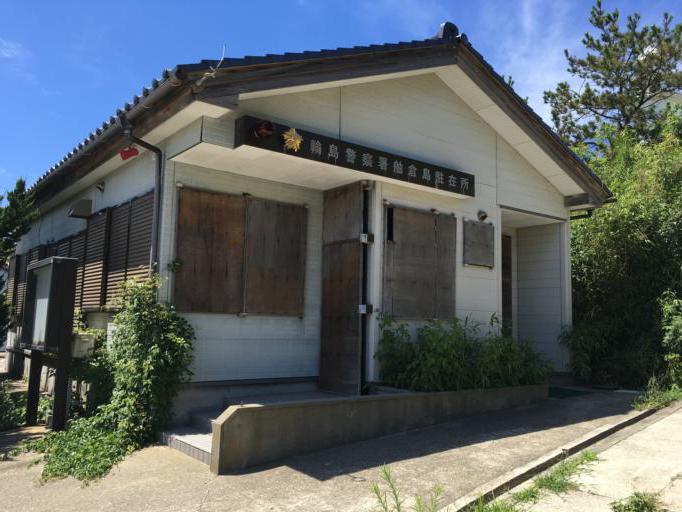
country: JP
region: Ishikawa
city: Nanao
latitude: 37.8508
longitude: 136.9189
